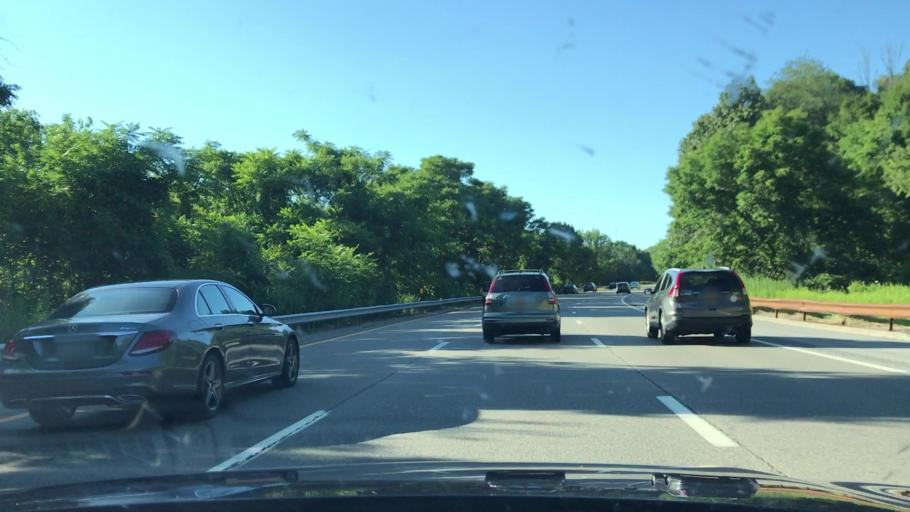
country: US
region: New York
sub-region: Westchester County
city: Briarcliff Manor
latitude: 41.1944
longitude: -73.8068
